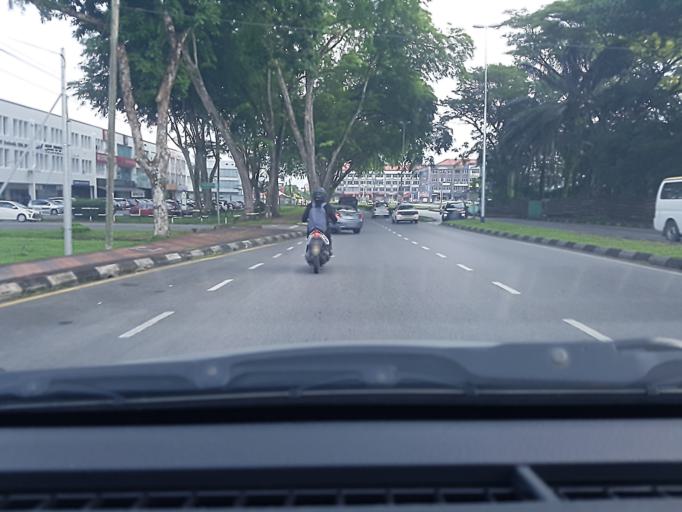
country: MY
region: Sarawak
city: Kuching
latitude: 1.5434
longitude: 110.3543
